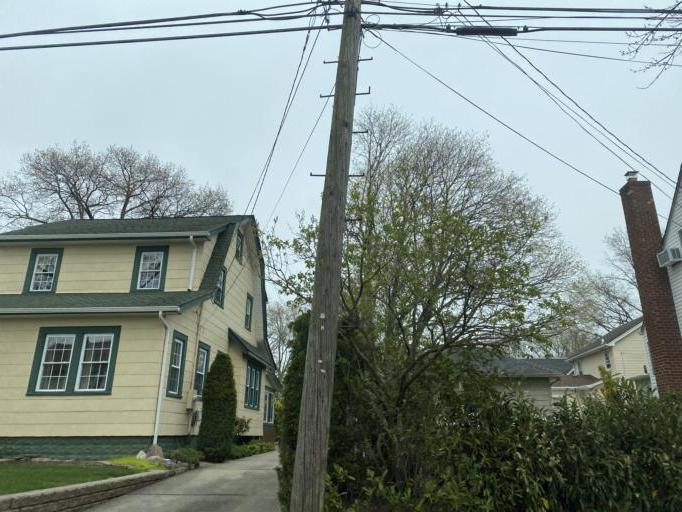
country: US
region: New York
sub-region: Nassau County
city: Bellerose
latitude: 40.7213
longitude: -73.7106
